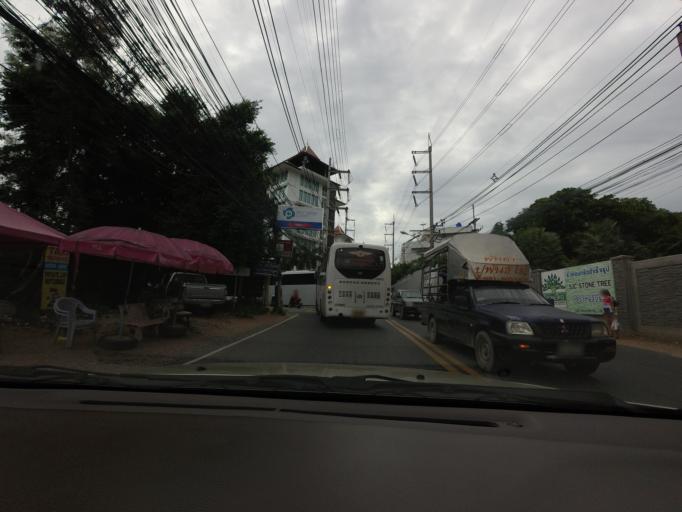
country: TH
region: Chon Buri
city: Phatthaya
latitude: 12.9121
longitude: 100.8685
